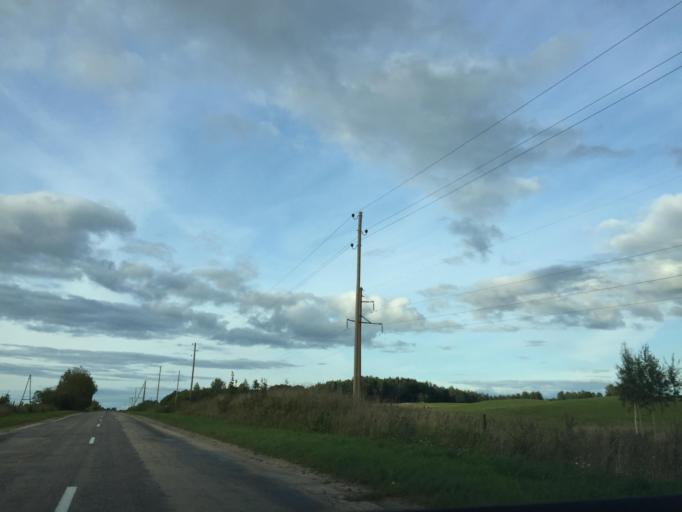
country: LV
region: Nereta
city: Nereta
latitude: 56.2286
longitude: 25.3223
